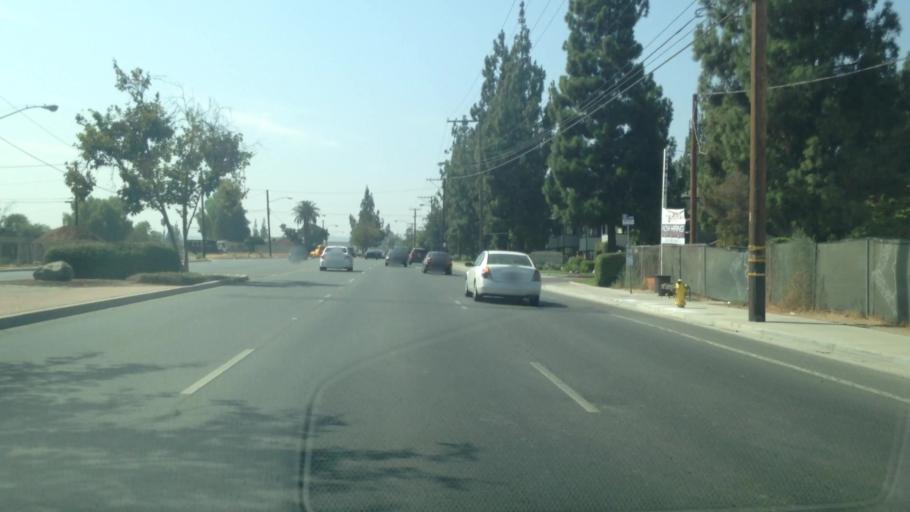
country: US
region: California
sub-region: Riverside County
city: Pedley
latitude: 33.9333
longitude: -117.4541
